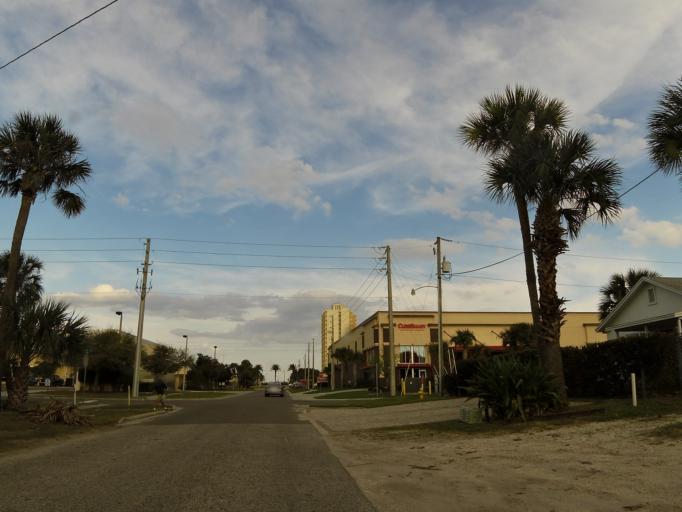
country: US
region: Florida
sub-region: Duval County
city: Jacksonville Beach
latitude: 30.2867
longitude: -81.3943
